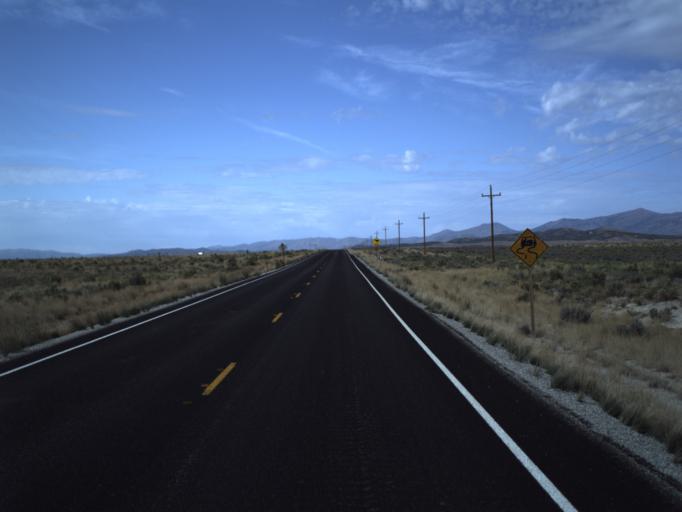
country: US
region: Idaho
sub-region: Cassia County
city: Burley
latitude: 41.7717
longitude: -113.4999
